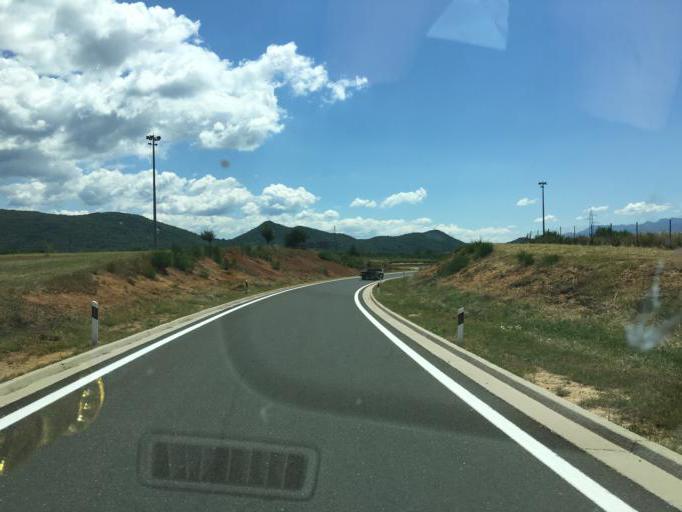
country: HR
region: Licko-Senjska
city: Gospic
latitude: 44.5730
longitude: 15.4254
